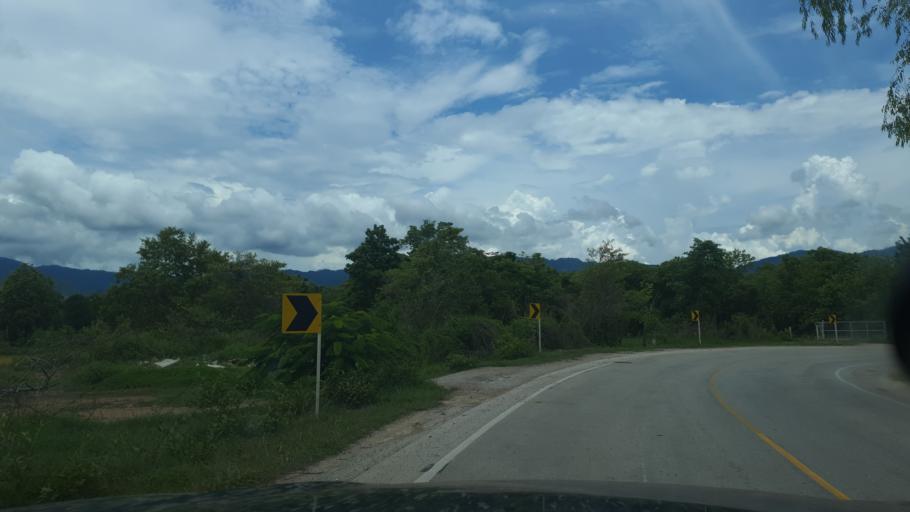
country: TH
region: Lampang
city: Sop Prap
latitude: 17.9186
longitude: 99.3877
